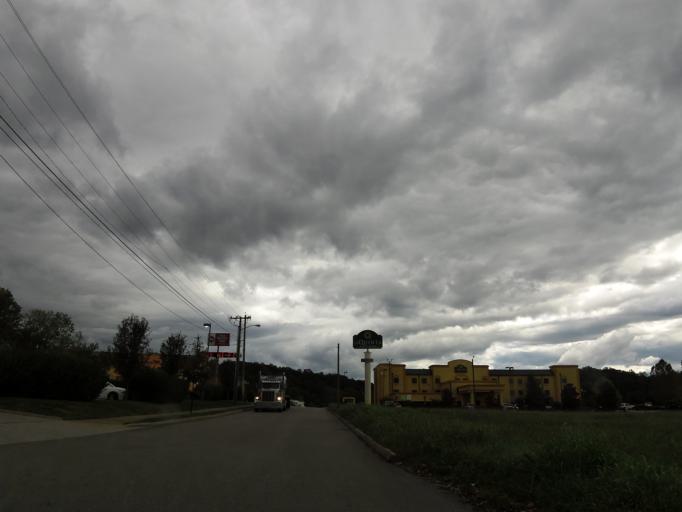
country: US
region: Tennessee
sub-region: Knox County
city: Mascot
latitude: 36.0001
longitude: -83.7753
